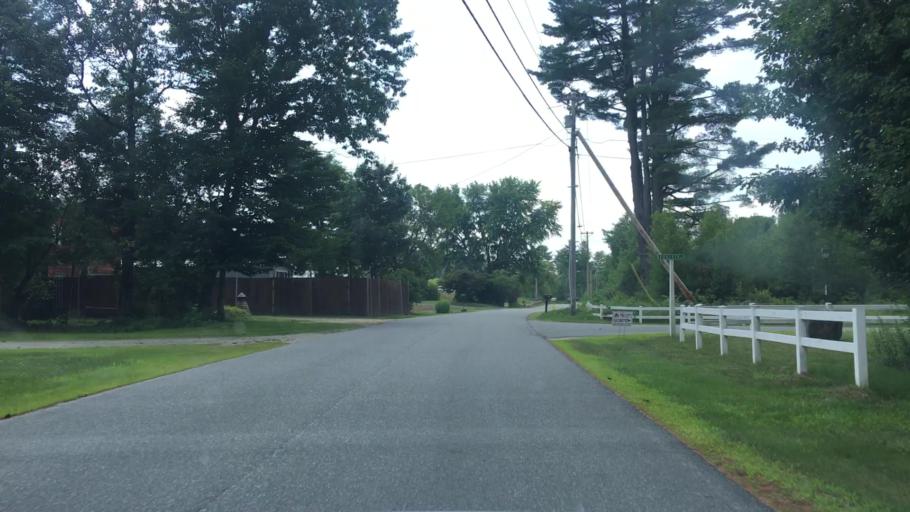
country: US
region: New Hampshire
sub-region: Grafton County
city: Enfield
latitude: 43.6778
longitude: -72.0956
